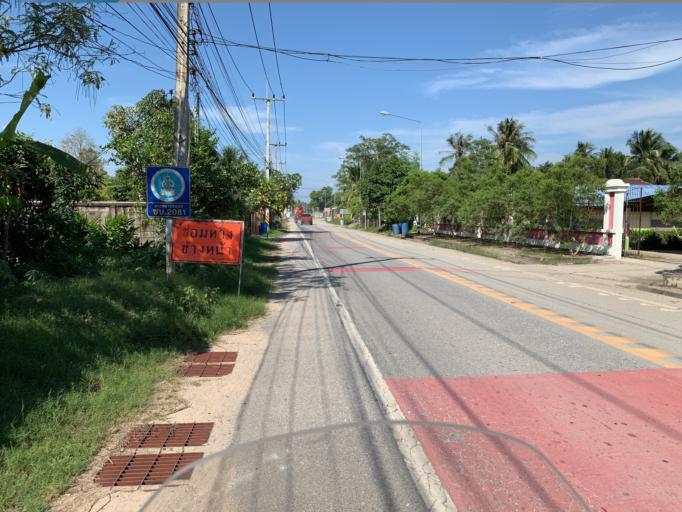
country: TH
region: Chon Buri
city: Phatthaya
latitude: 12.8675
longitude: 100.9709
